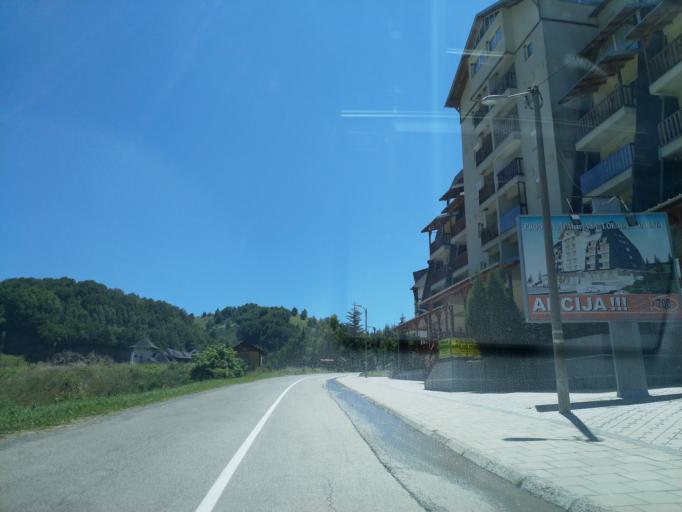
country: XK
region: Mitrovica
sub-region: Komuna e Leposaviqit
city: Leposaviq
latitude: 43.2886
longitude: 20.8800
